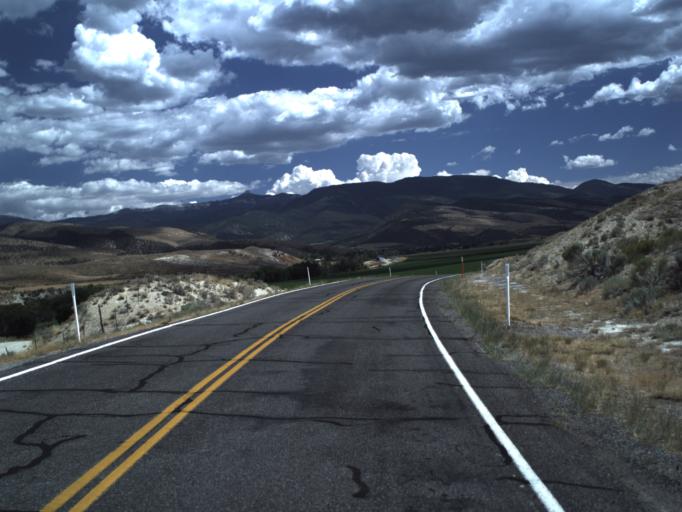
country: US
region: Utah
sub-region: Sanpete County
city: Gunnison
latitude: 39.1457
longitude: -111.7363
